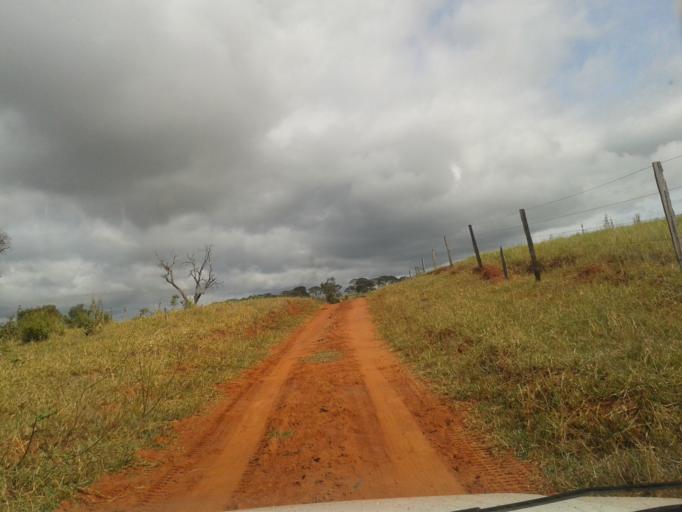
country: BR
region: Minas Gerais
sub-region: Campina Verde
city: Campina Verde
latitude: -19.4140
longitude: -49.6586
